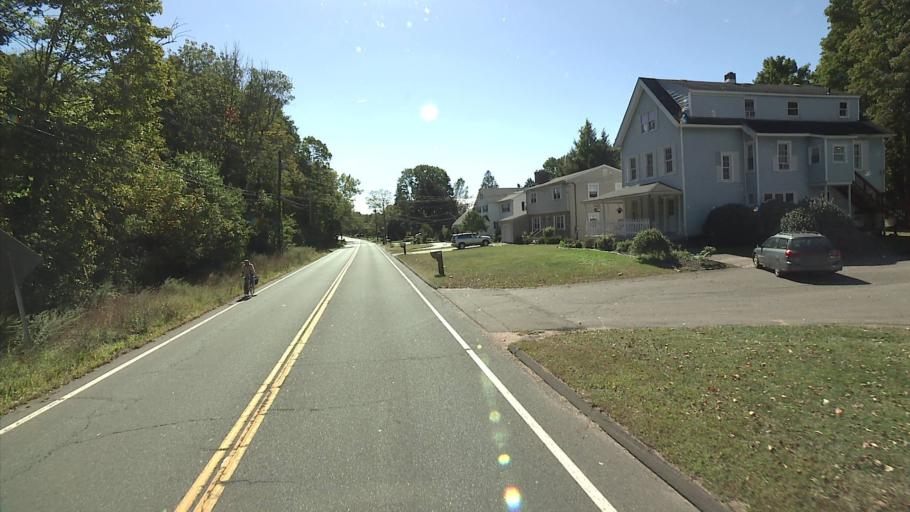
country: US
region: Connecticut
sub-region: New Haven County
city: Woodbridge
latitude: 41.3506
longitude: -72.9839
